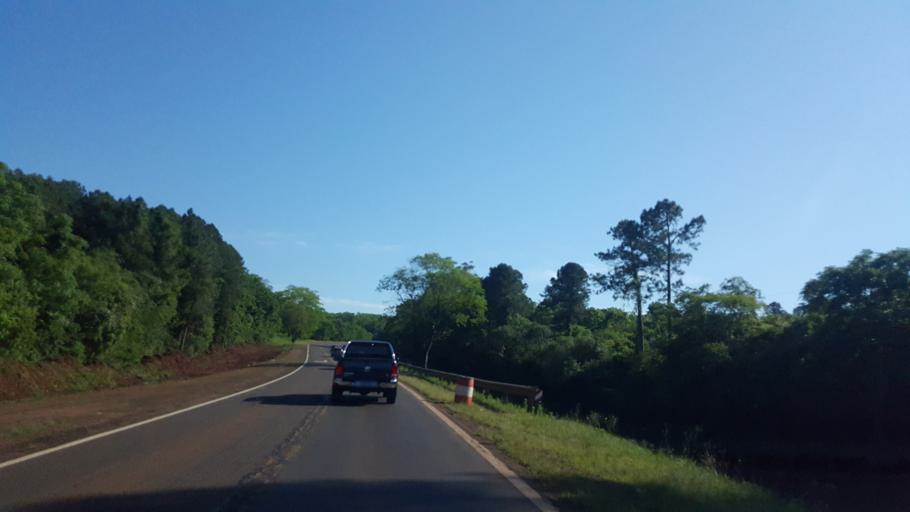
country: AR
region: Misiones
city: Santa Ana
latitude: -27.3625
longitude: -55.5575
